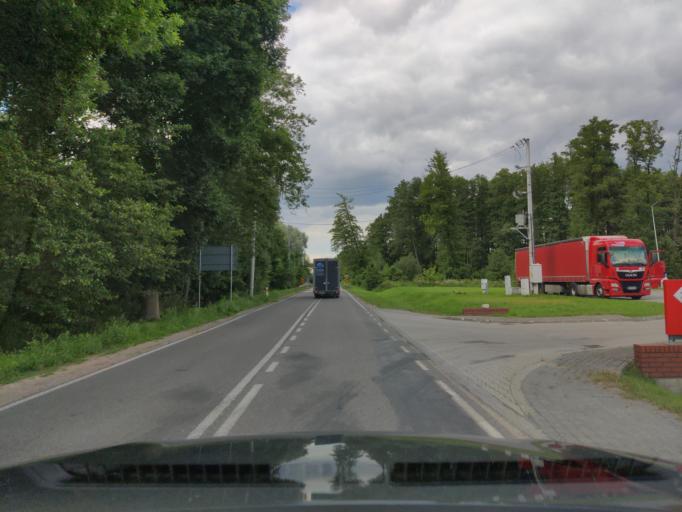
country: PL
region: Masovian Voivodeship
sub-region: Powiat sokolowski
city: Kosow Lacki
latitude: 52.5843
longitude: 22.1537
